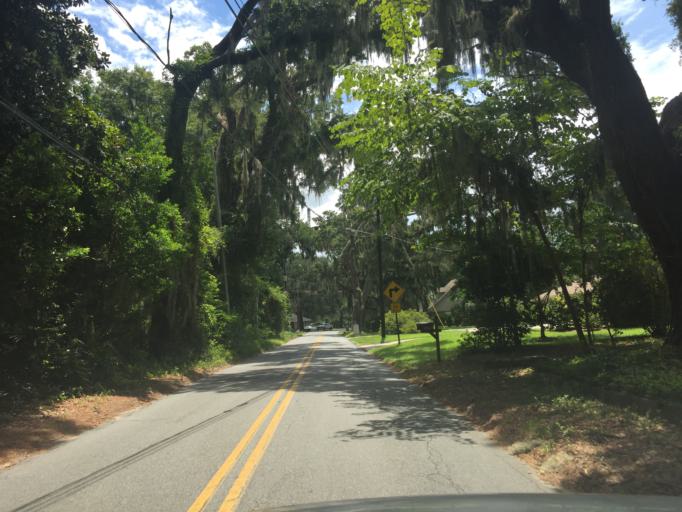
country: US
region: Georgia
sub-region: Chatham County
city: Montgomery
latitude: 31.9422
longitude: -81.1077
